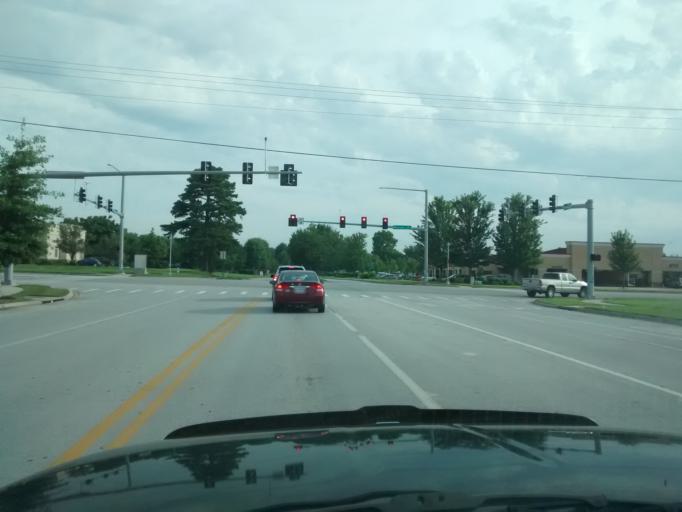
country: US
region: Arkansas
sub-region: Washington County
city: Farmington
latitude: 36.0780
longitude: -94.2083
